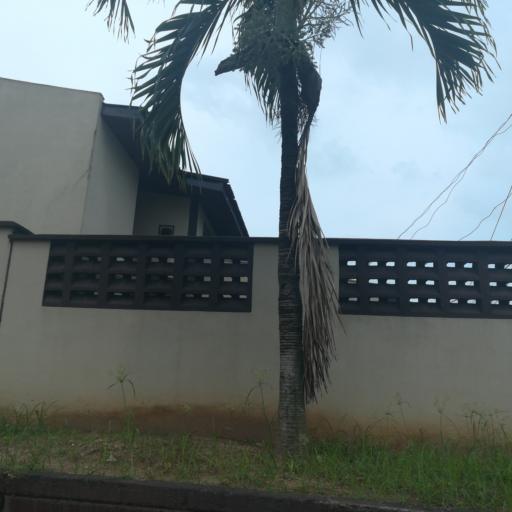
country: NG
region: Lagos
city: Ojota
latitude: 6.5762
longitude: 3.3925
